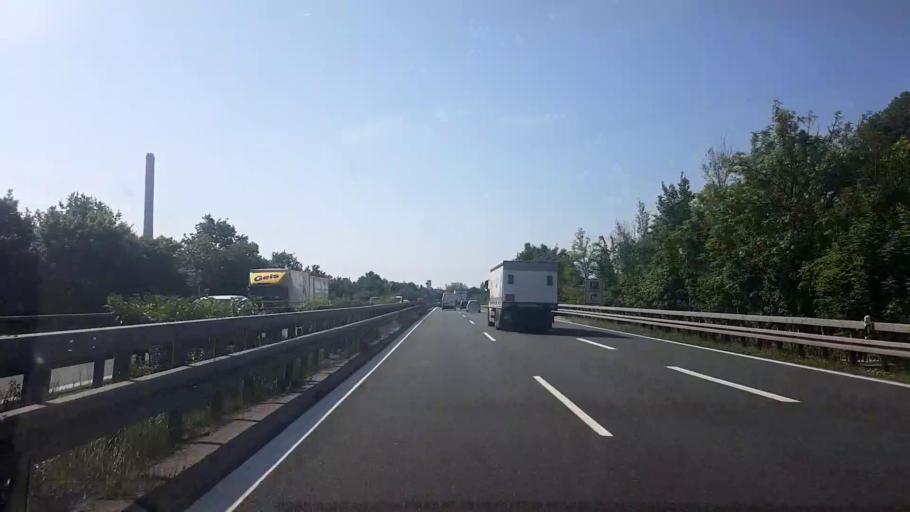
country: DE
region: Bavaria
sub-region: Regierungsbezirk Mittelfranken
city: Erlangen
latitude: 49.5990
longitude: 10.9982
